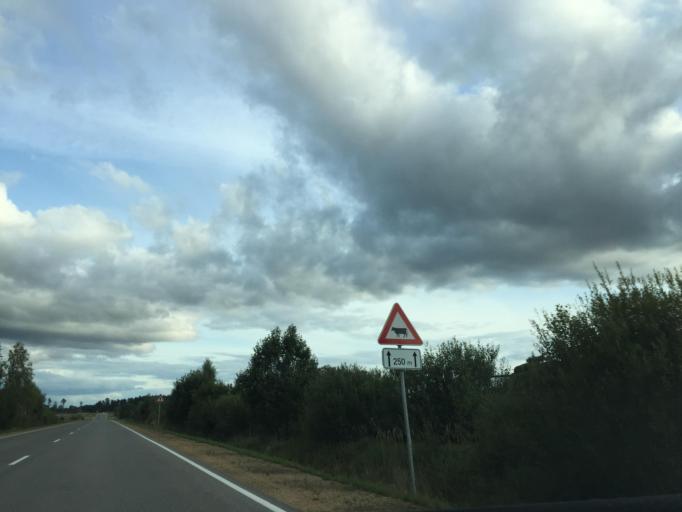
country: LV
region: Nereta
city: Nereta
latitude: 56.2344
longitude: 25.2718
